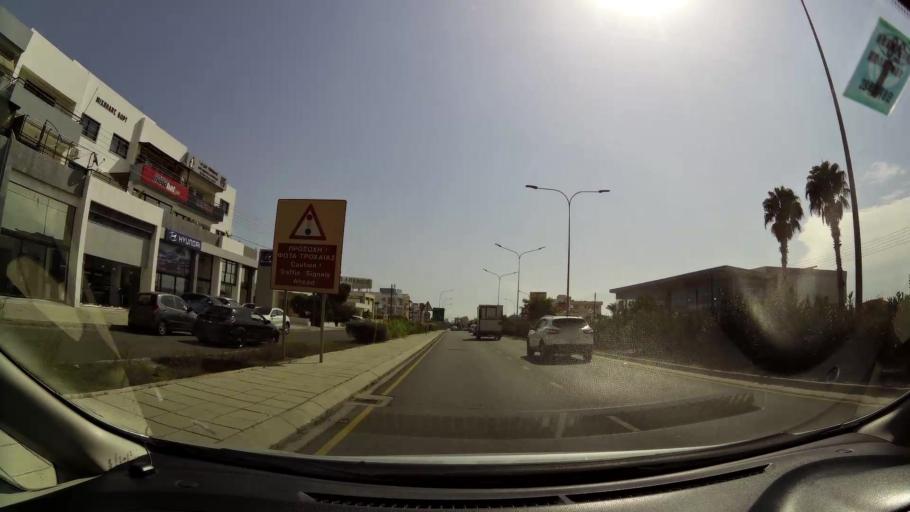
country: CY
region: Larnaka
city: Aradippou
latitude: 34.9341
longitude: 33.5940
